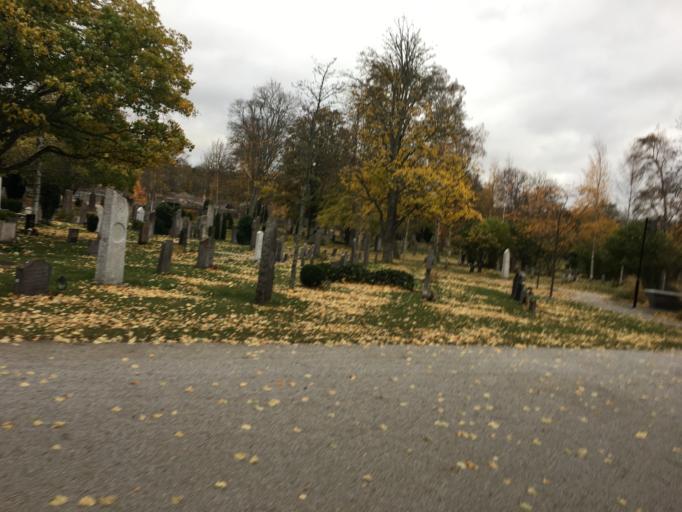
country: SE
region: Gotland
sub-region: Gotland
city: Visby
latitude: 57.6588
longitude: 18.3159
